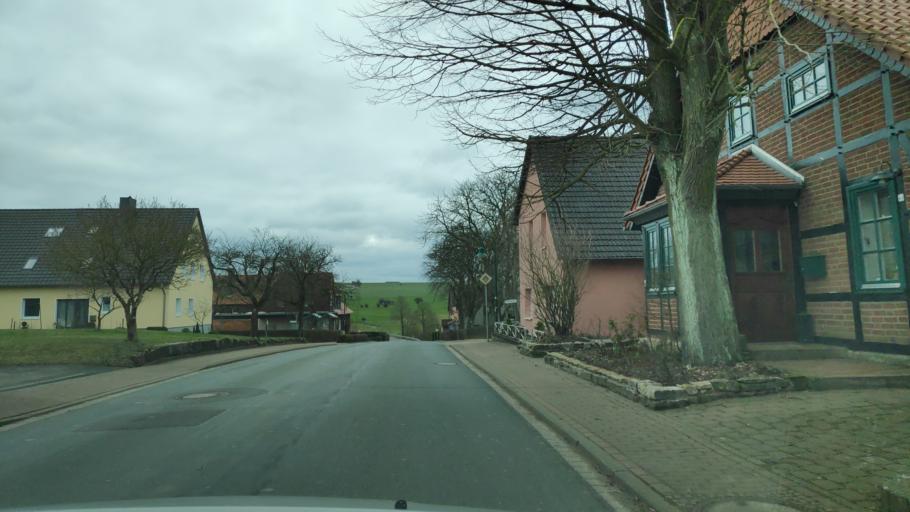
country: DE
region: Lower Saxony
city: Rehren
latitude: 52.2320
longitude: 9.2799
